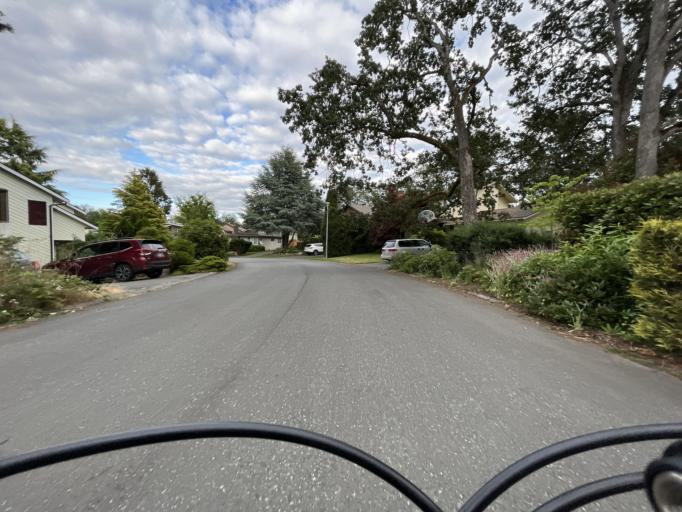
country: CA
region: British Columbia
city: Oak Bay
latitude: 48.4833
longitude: -123.3420
